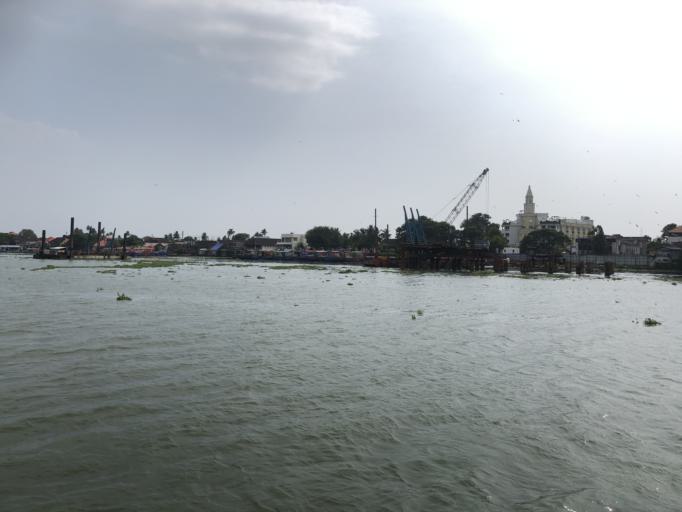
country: IN
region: Kerala
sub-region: Ernakulam
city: Cochin
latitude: 9.9694
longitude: 76.2536
